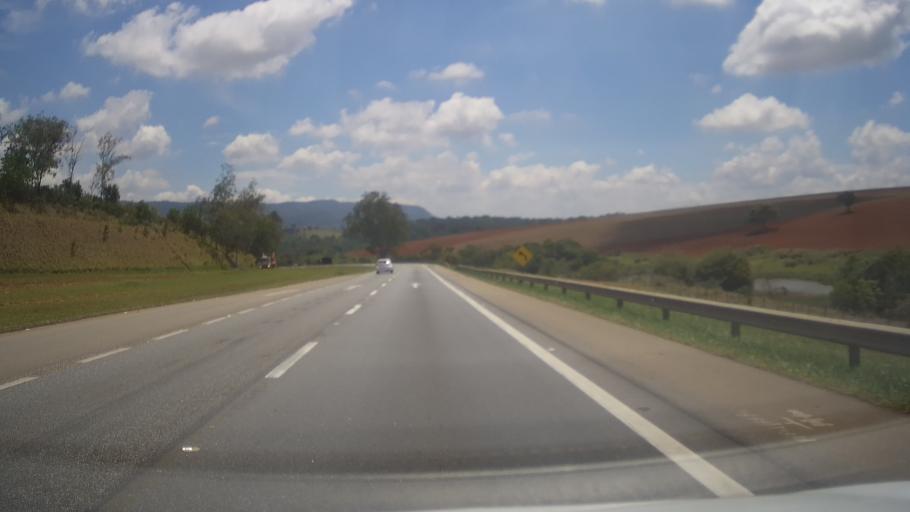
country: BR
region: Minas Gerais
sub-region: Sao Goncalo Do Sapucai
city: Sao Goncalo do Sapucai
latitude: -21.9305
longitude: -45.6117
